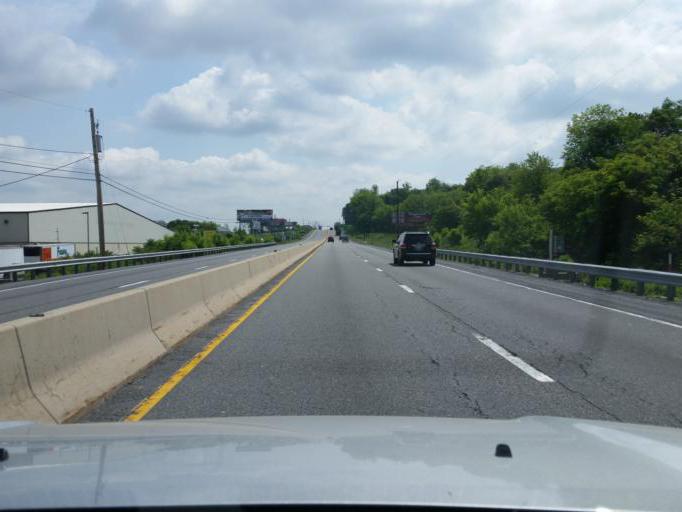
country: US
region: Pennsylvania
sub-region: Dauphin County
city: Lawnton
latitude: 40.2579
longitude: -76.7857
